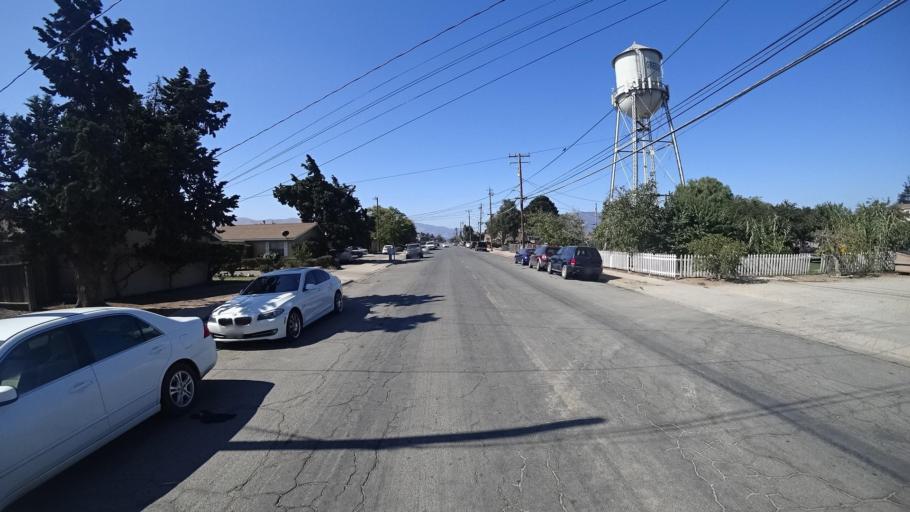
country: US
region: California
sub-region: Monterey County
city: Greenfield
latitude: 36.3177
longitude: -121.2490
